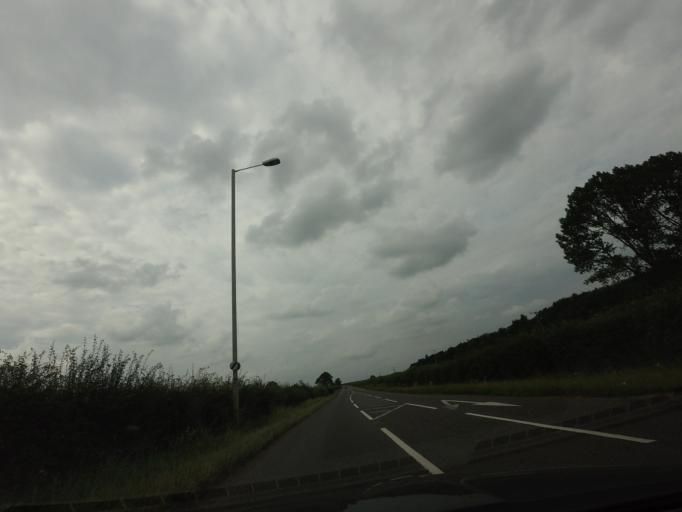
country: GB
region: England
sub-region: Shropshire
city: Tong
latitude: 52.6713
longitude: -2.3093
